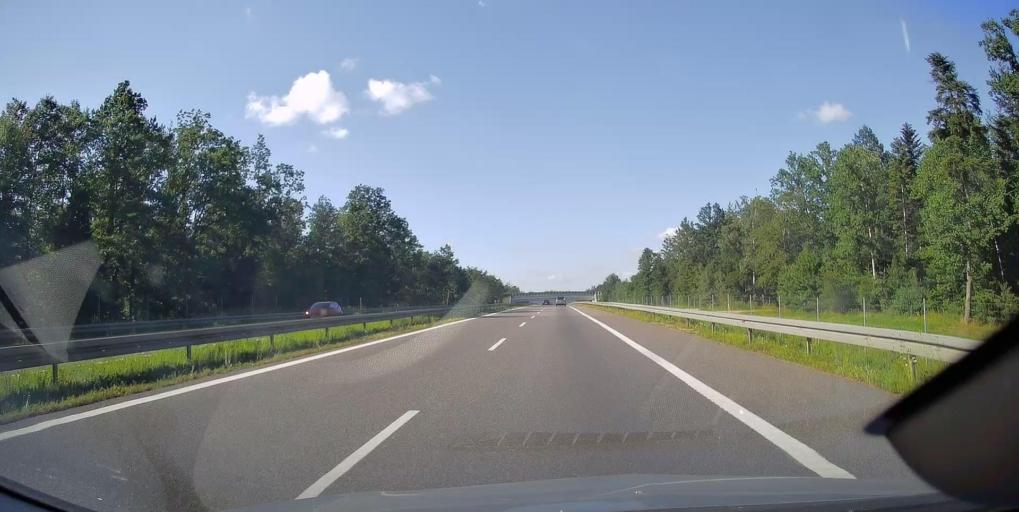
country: PL
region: Swietokrzyskie
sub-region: Powiat skarzyski
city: Suchedniow
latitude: 51.0740
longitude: 20.8367
